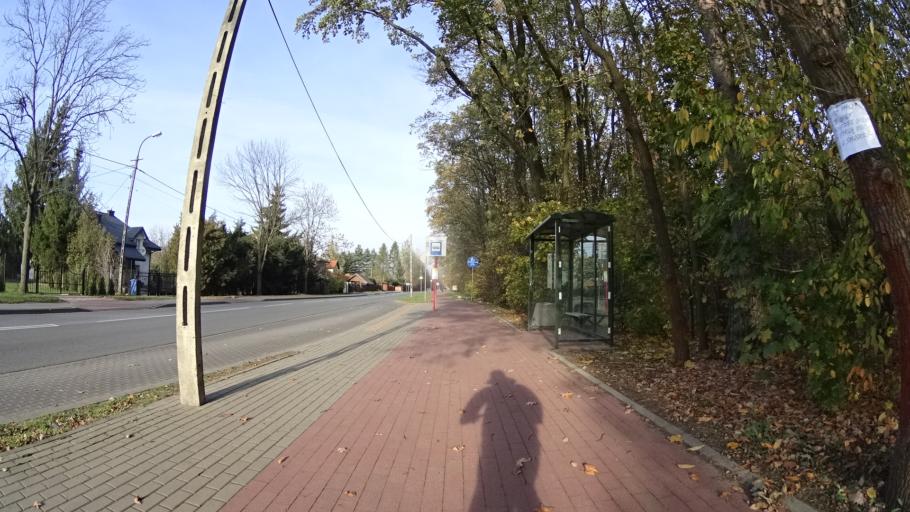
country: PL
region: Masovian Voivodeship
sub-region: Powiat warszawski zachodni
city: Babice
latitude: 52.2651
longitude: 20.8575
